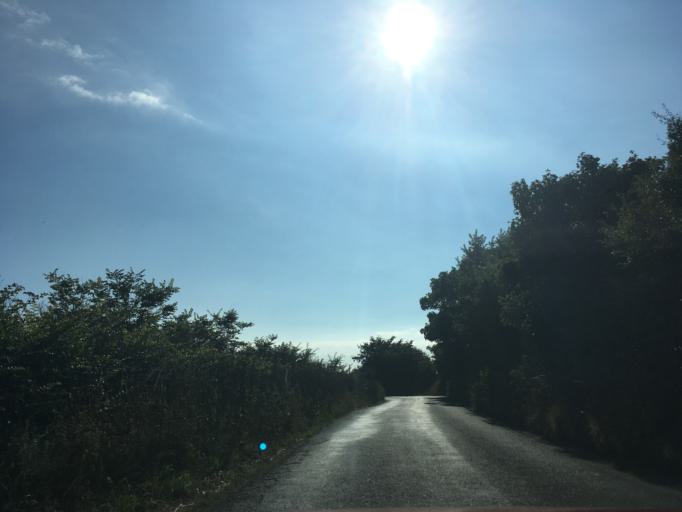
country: IE
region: Leinster
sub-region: Loch Garman
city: Rosslare
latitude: 52.2297
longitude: -6.4320
